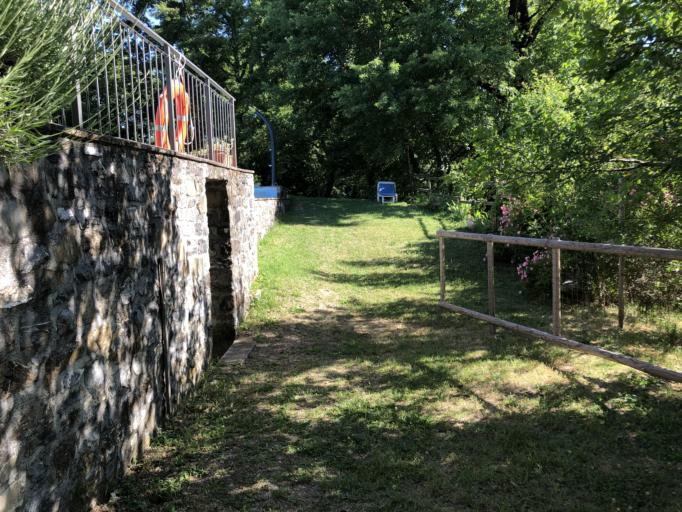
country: IT
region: Tuscany
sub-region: Province of Pisa
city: Castelnuovo di Val di Cecina
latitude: 43.2046
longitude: 10.9253
